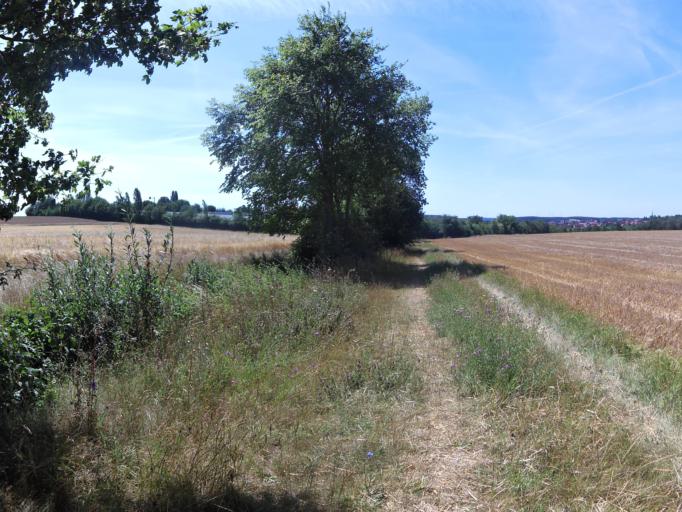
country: DE
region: Bavaria
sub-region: Regierungsbezirk Unterfranken
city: Hettstadt
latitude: 49.8097
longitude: 9.8330
